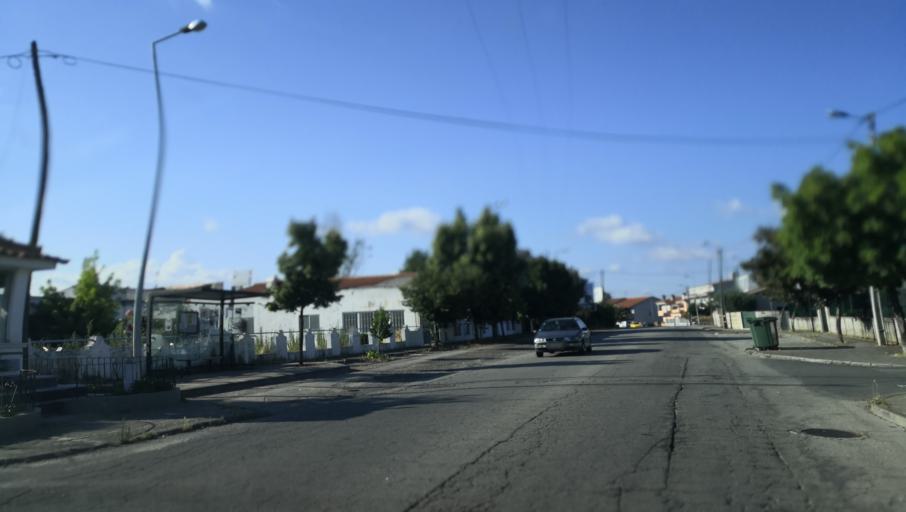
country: PT
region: Vila Real
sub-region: Chaves
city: Chaves
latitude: 41.7624
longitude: -7.4673
